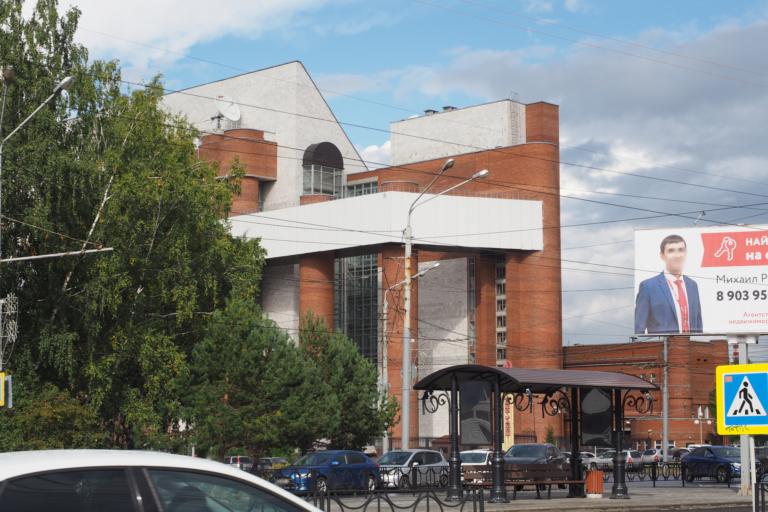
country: RU
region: Tomsk
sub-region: Tomskiy Rayon
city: Tomsk
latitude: 56.4661
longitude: 84.9803
